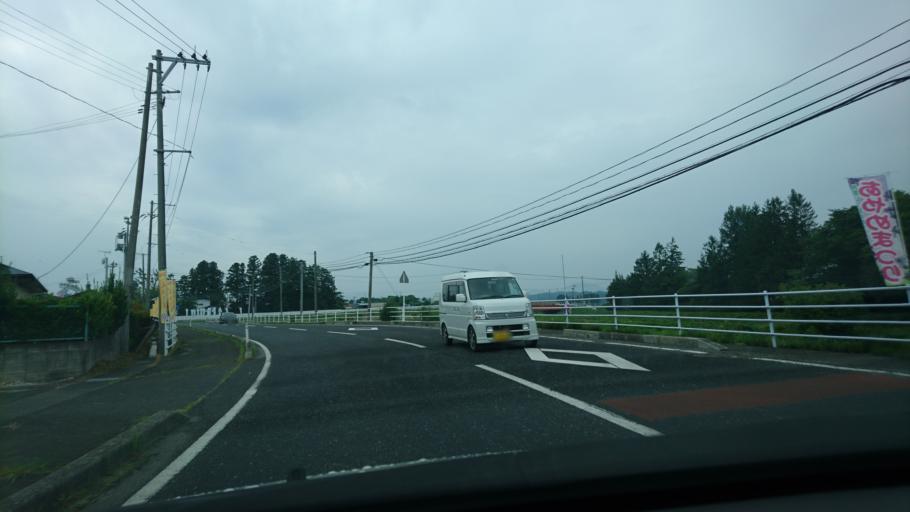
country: JP
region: Miyagi
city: Furukawa
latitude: 38.7397
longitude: 140.9483
